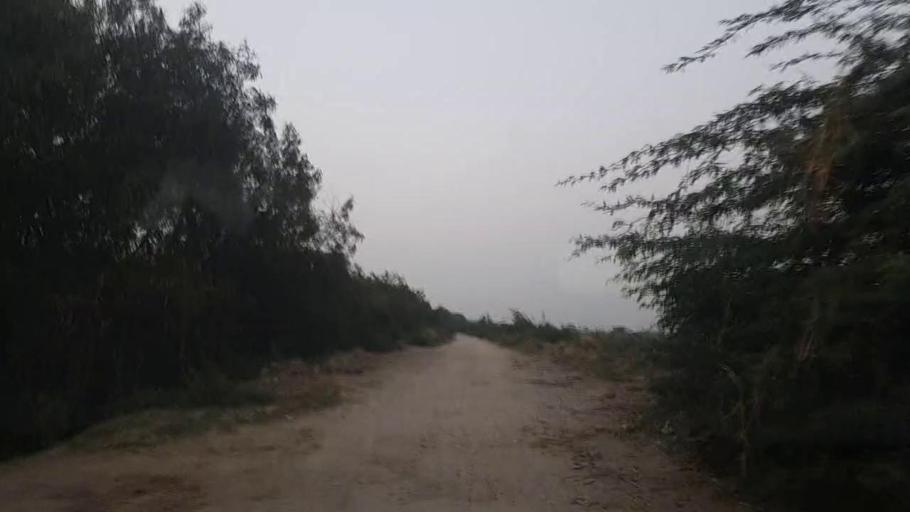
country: PK
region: Sindh
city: Mirpur Sakro
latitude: 24.5807
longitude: 67.7853
